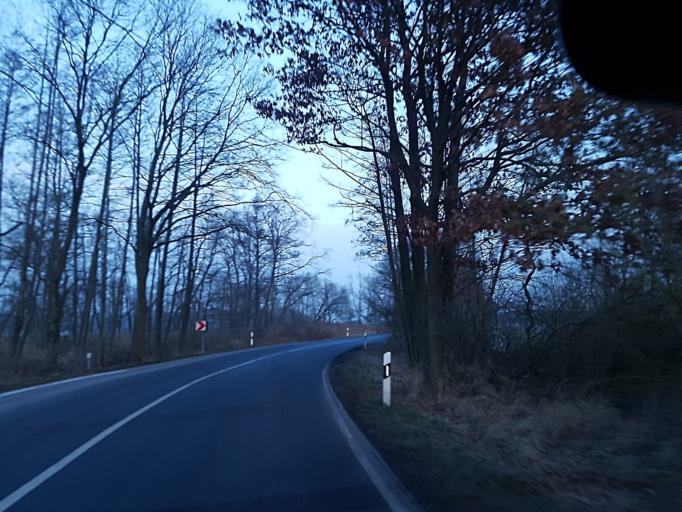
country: DE
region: Saxony-Anhalt
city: Holzdorf
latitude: 51.7455
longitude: 13.1584
